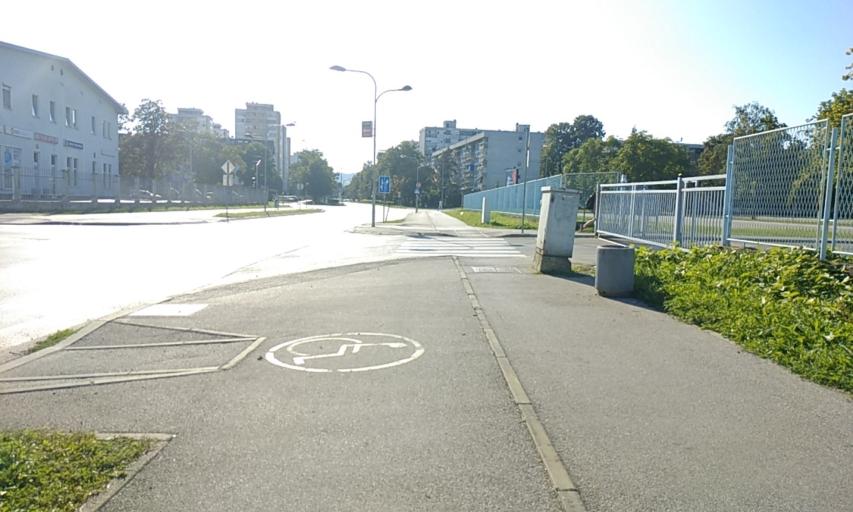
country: BA
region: Republika Srpska
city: Starcevica
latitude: 44.7723
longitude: 17.2103
